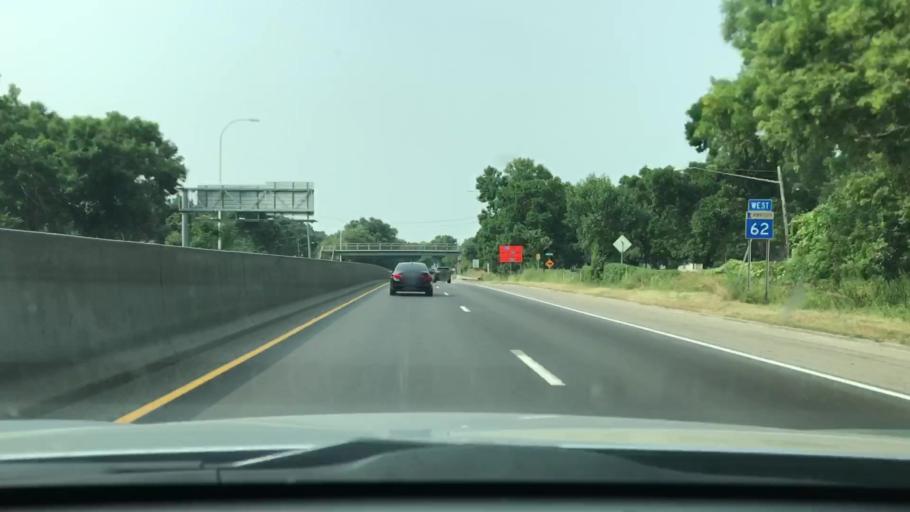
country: US
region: Minnesota
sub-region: Hennepin County
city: Richfield
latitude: 44.8930
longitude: -93.2544
